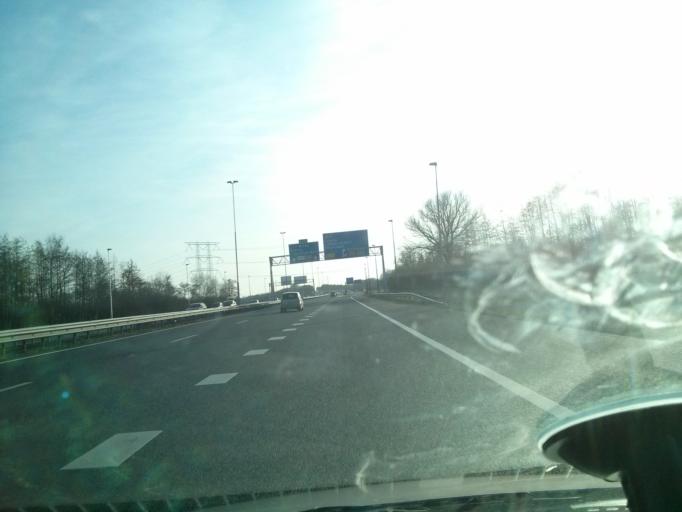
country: NL
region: North Brabant
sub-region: Gemeente Tilburg
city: Tilburg
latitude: 51.5607
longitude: 5.1345
